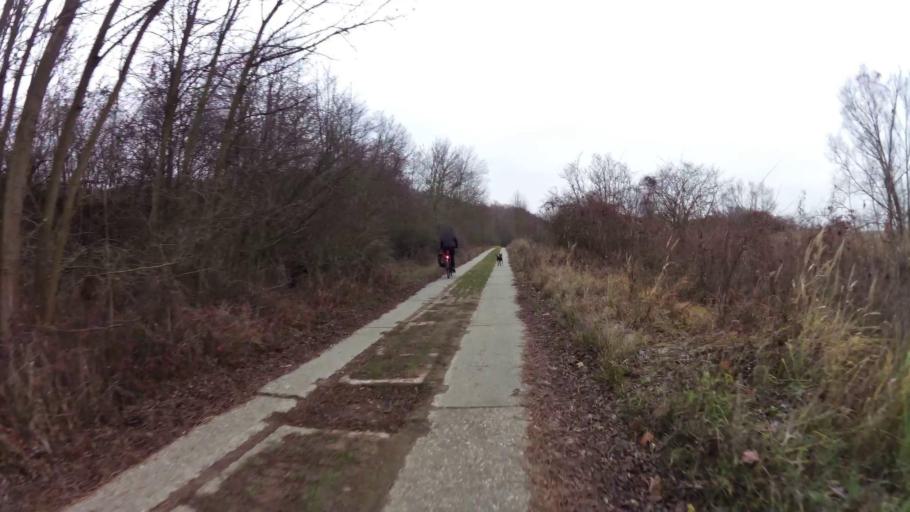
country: PL
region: West Pomeranian Voivodeship
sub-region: Powiat gryfinski
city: Cedynia
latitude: 52.9320
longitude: 14.1489
